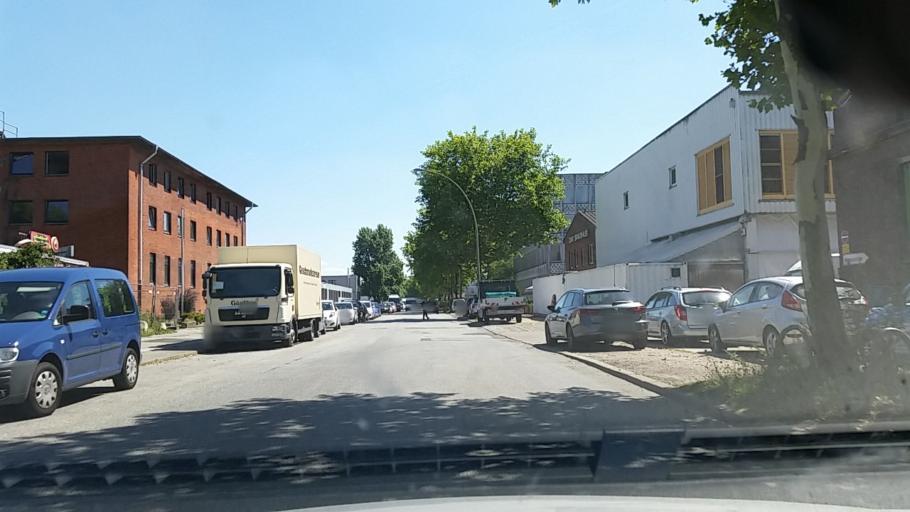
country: DE
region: Hamburg
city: Rothenburgsort
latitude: 53.5358
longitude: 10.0584
